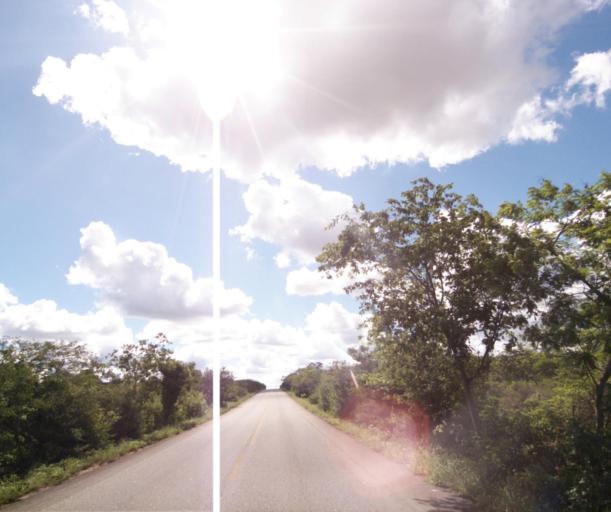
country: BR
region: Bahia
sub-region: Caetite
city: Caetite
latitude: -14.1675
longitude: -42.2481
